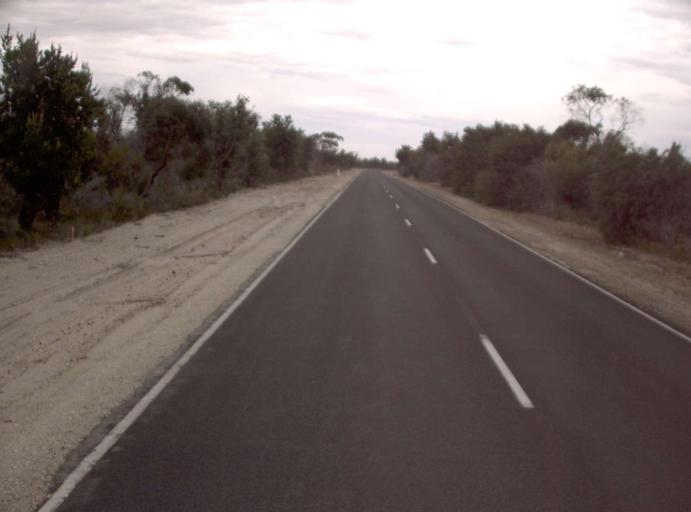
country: AU
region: Victoria
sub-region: East Gippsland
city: Bairnsdale
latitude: -38.1109
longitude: 147.4693
